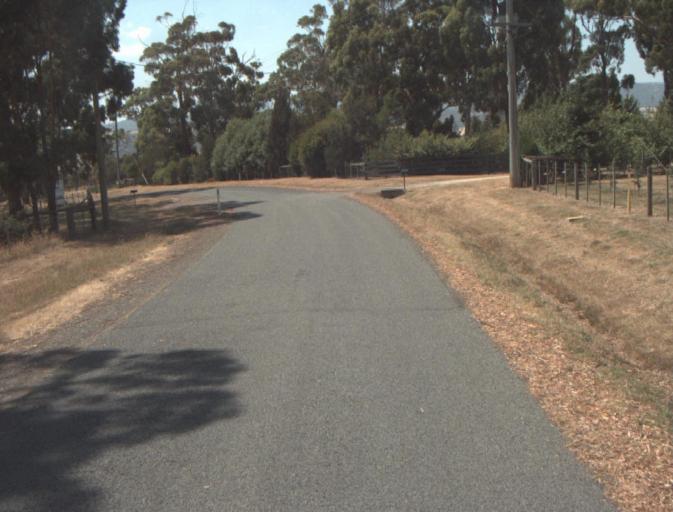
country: AU
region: Tasmania
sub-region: Launceston
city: Newstead
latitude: -41.4993
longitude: 147.2118
